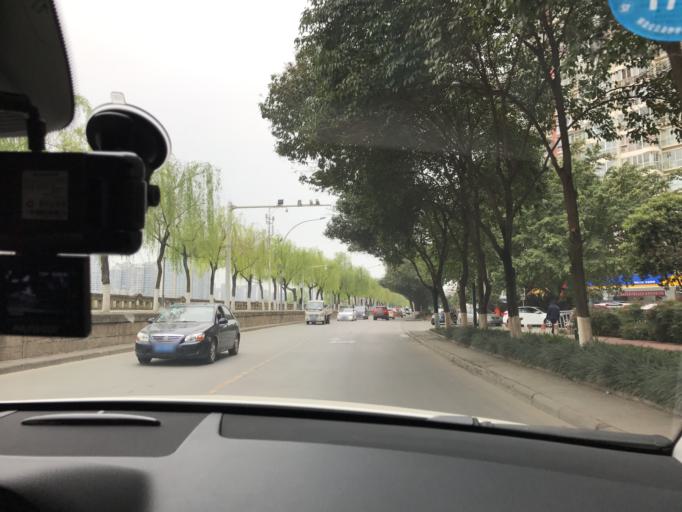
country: CN
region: Sichuan
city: Mianyang
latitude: 31.4530
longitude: 104.7102
